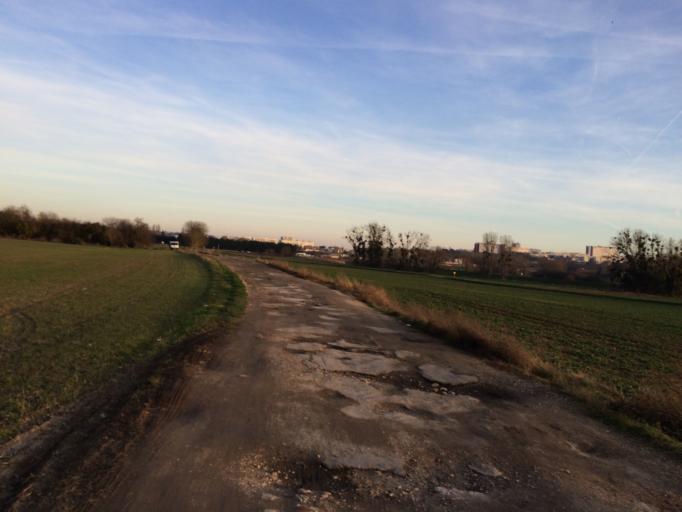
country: FR
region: Ile-de-France
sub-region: Departement de l'Essonne
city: Champlan
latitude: 48.7024
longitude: 2.2772
